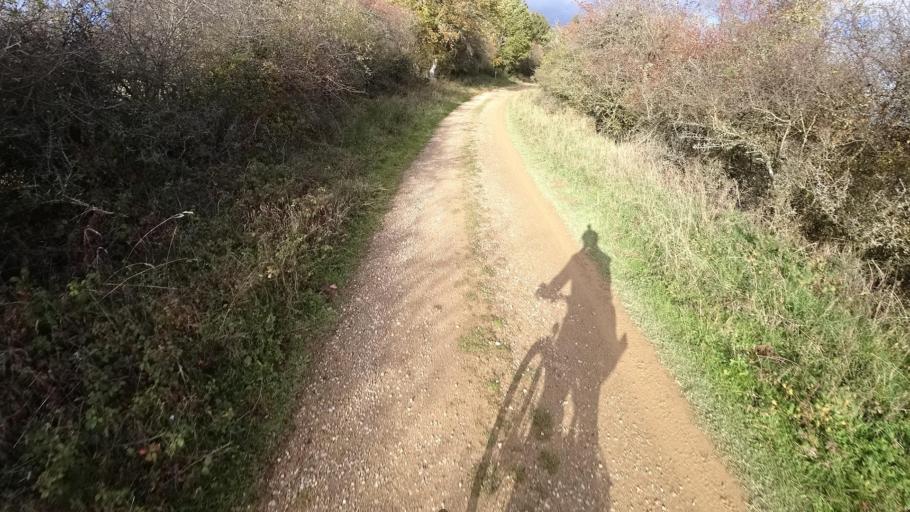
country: DE
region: Rheinland-Pfalz
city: Honningen
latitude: 50.4662
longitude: 6.9398
